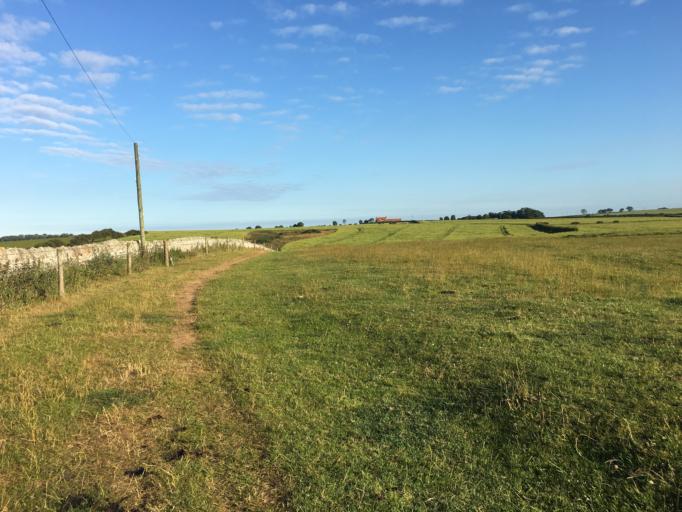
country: GB
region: England
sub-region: Northumberland
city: Bamburgh
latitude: 55.5975
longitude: -1.6944
